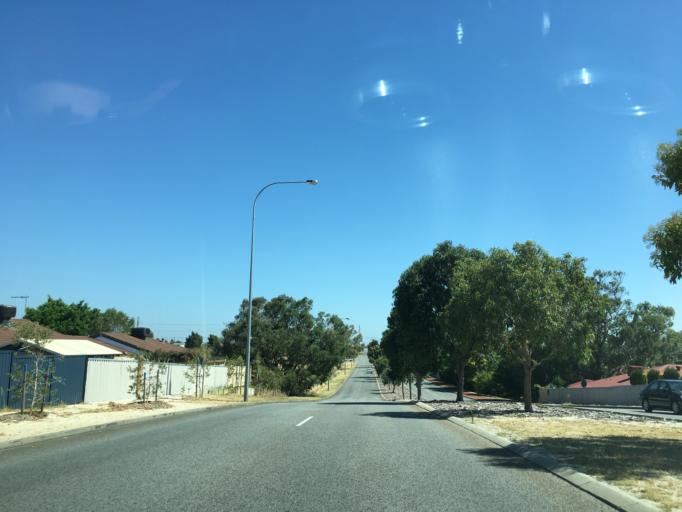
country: AU
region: Western Australia
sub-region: Canning
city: Canning Vale
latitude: -32.0507
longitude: 115.9043
